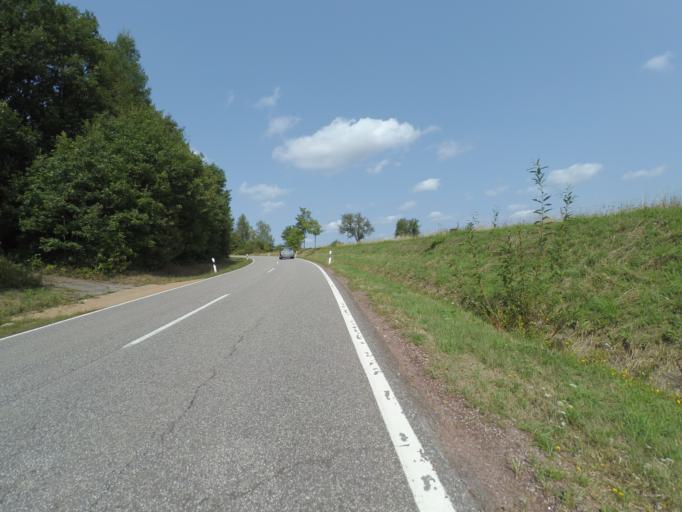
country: DE
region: Saarland
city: Britten
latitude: 49.5139
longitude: 6.6905
